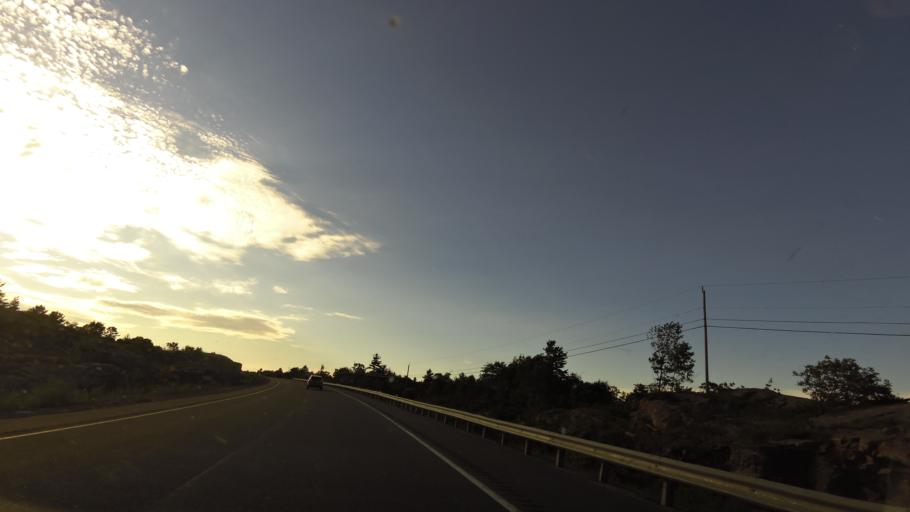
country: CA
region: Ontario
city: Midland
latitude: 44.8920
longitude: -79.7570
